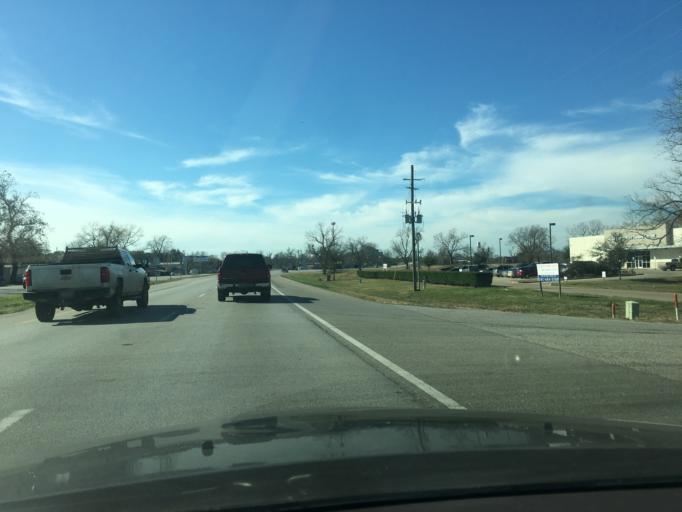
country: US
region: Texas
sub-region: Fort Bend County
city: Richmond
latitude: 29.5872
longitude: -95.7510
